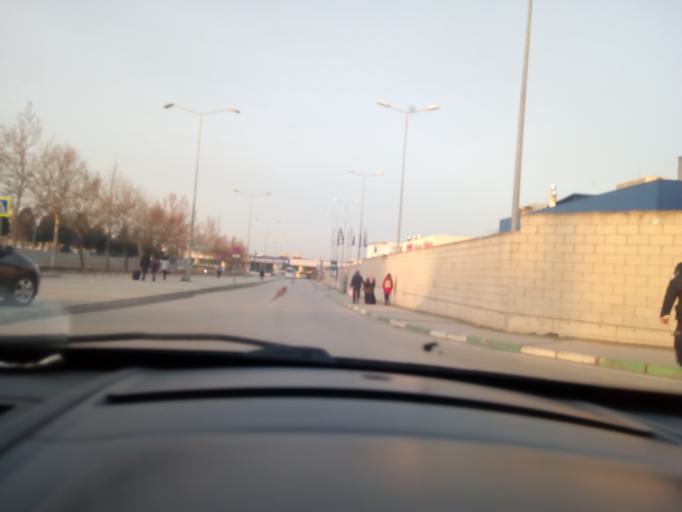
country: TR
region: Bursa
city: Demirtas
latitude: 40.2664
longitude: 29.0567
